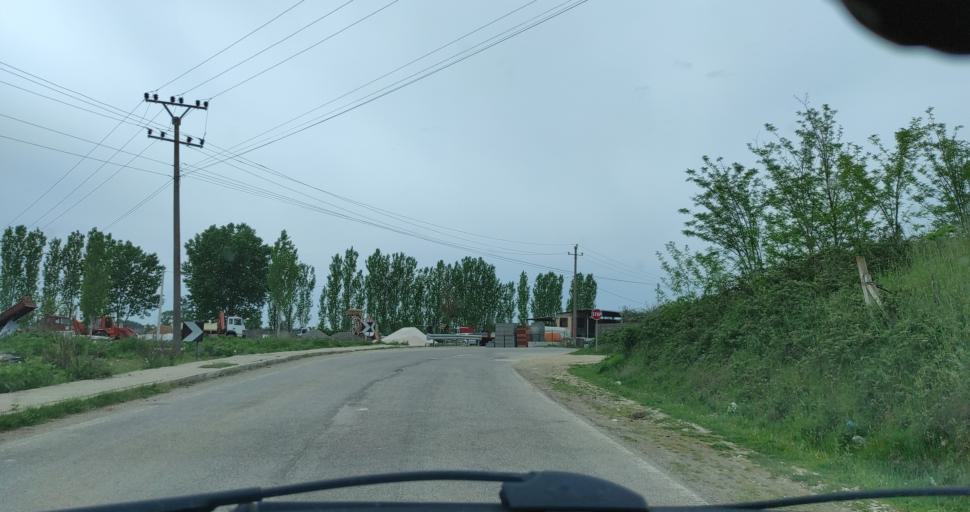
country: AL
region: Lezhe
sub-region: Rrethi i Kurbinit
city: Lac
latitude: 41.6121
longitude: 19.7117
